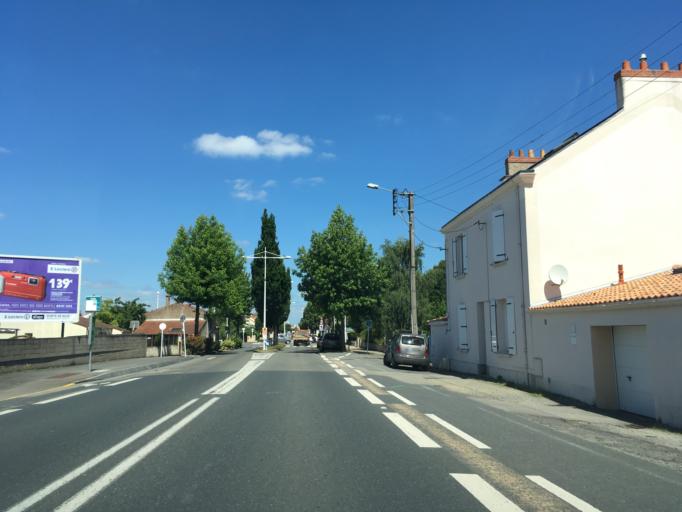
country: FR
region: Pays de la Loire
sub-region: Departement de la Loire-Atlantique
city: Les Sorinieres
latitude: 47.1453
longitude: -1.5274
